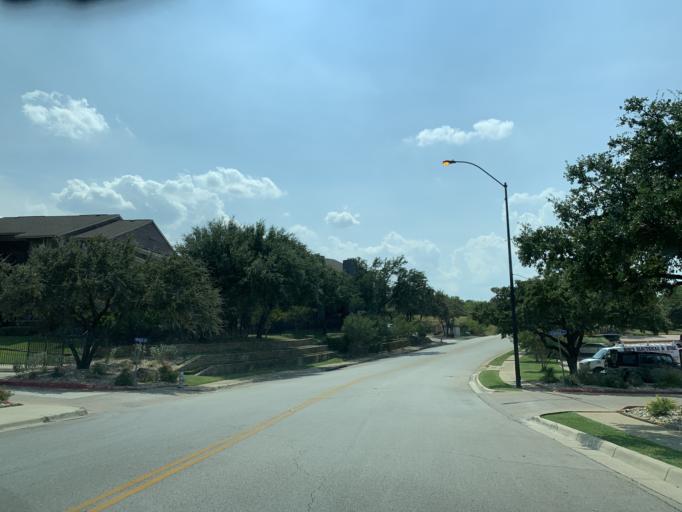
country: US
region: Texas
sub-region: Tarrant County
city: Richland Hills
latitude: 32.7683
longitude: -97.2159
